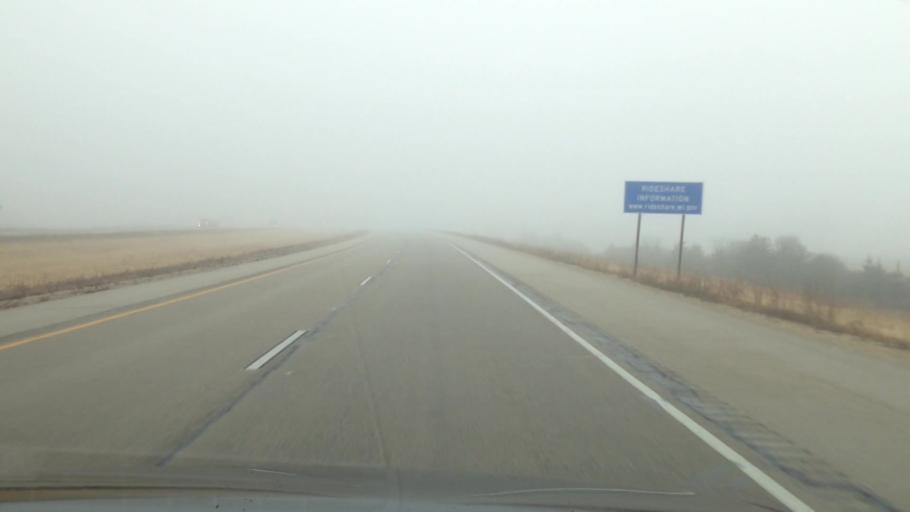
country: US
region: Wisconsin
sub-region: Walworth County
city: Elkhorn
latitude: 42.7028
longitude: -88.4877
